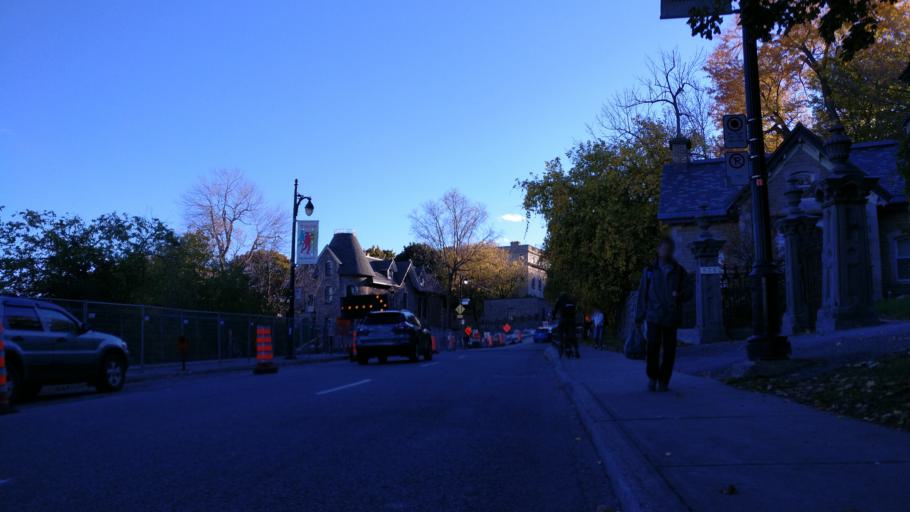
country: CA
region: Quebec
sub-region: Montreal
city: Montreal
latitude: 45.5059
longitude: -73.5812
